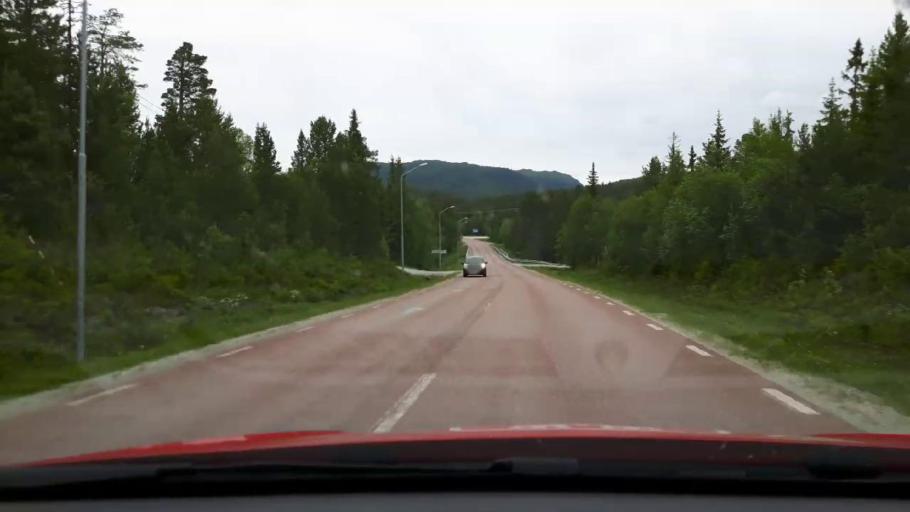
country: SE
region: Jaemtland
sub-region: Are Kommun
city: Are
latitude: 62.5535
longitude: 12.5667
